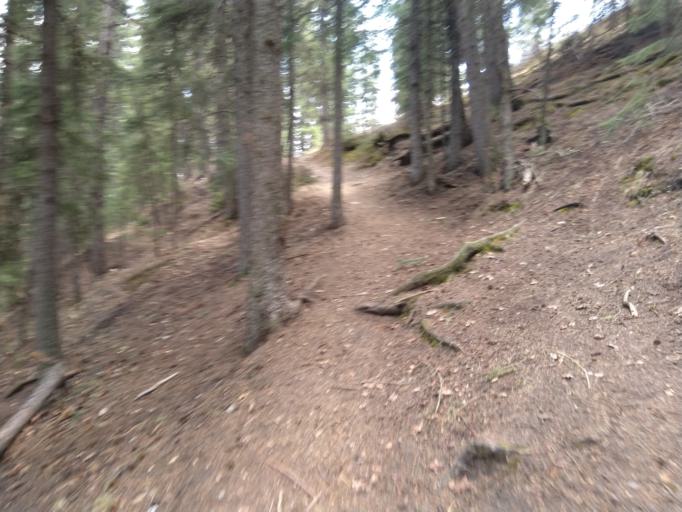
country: CA
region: Alberta
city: Cochrane
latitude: 51.1903
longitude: -114.5119
